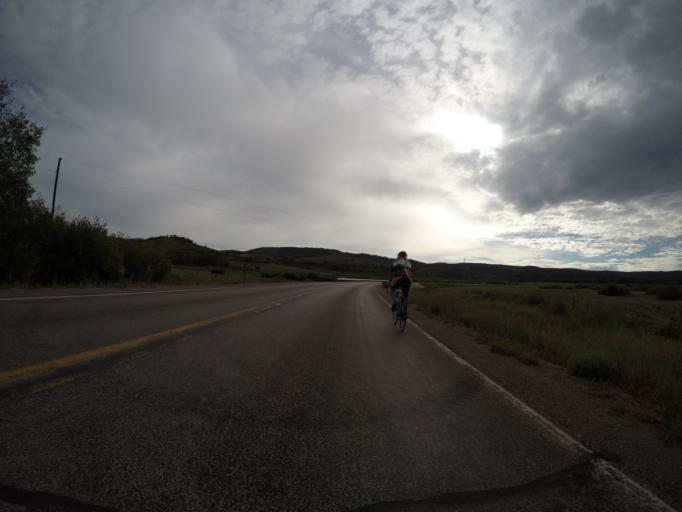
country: US
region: Wyoming
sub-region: Carbon County
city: Saratoga
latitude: 41.3654
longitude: -106.5580
